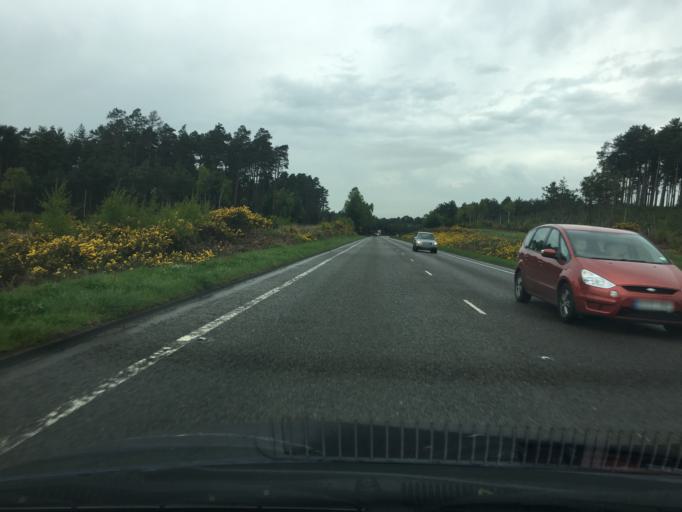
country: GB
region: England
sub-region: Bracknell Forest
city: Crowthorne
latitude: 51.3775
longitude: -0.7702
